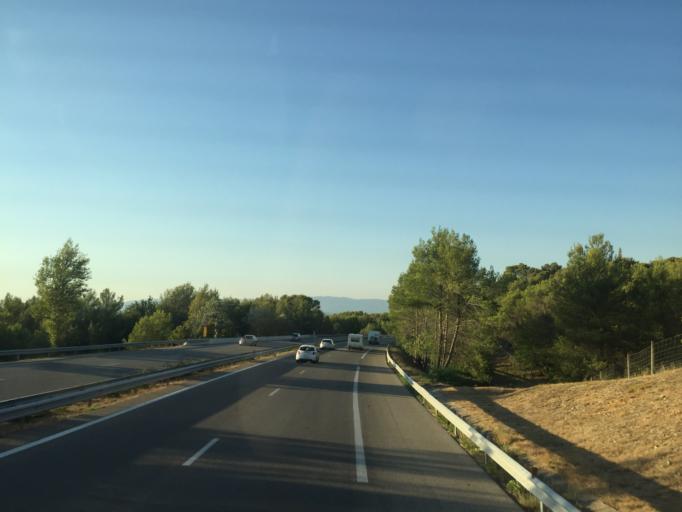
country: FR
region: Provence-Alpes-Cote d'Azur
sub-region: Departement des Bouches-du-Rhone
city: Venelles
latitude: 43.6243
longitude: 5.4924
